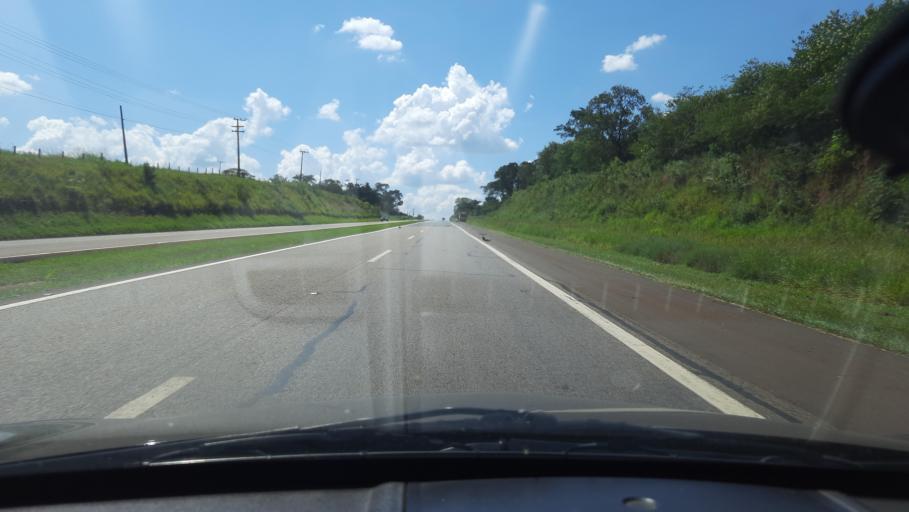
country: BR
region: Sao Paulo
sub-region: Casa Branca
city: Casa Branca
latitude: -21.7292
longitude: -47.0760
